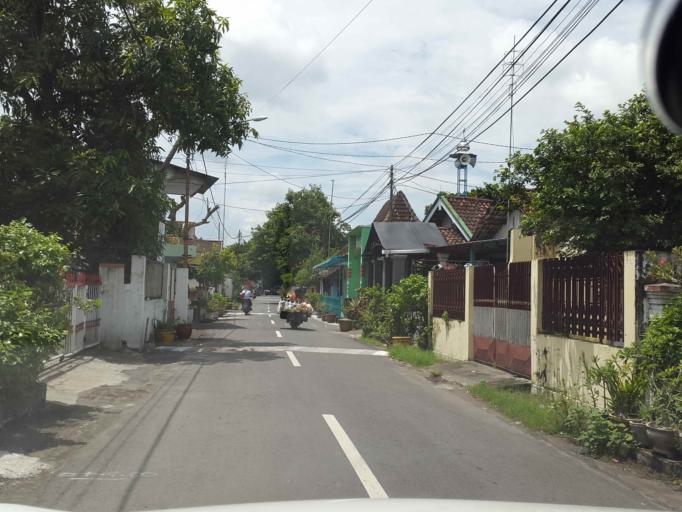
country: ID
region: East Java
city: Mojokerto
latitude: -7.4547
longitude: 112.4482
